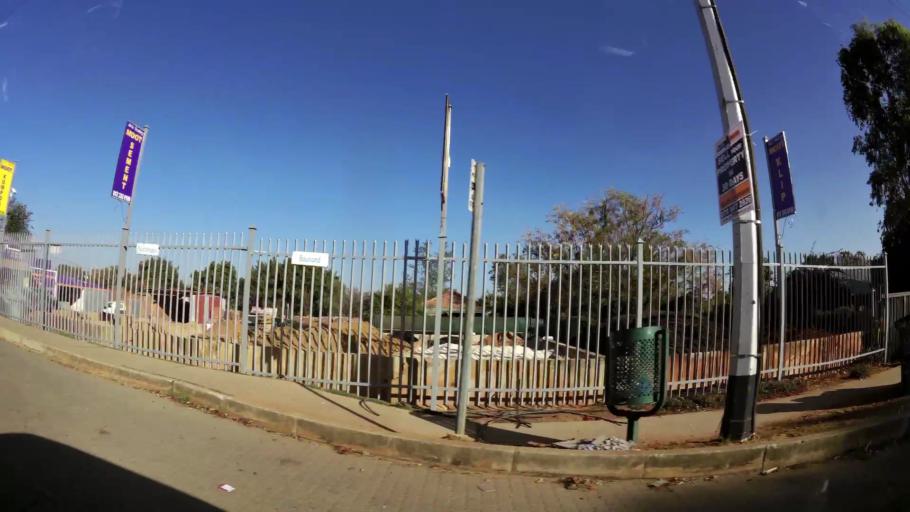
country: ZA
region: Gauteng
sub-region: City of Tshwane Metropolitan Municipality
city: Pretoria
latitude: -25.6976
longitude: 28.2383
